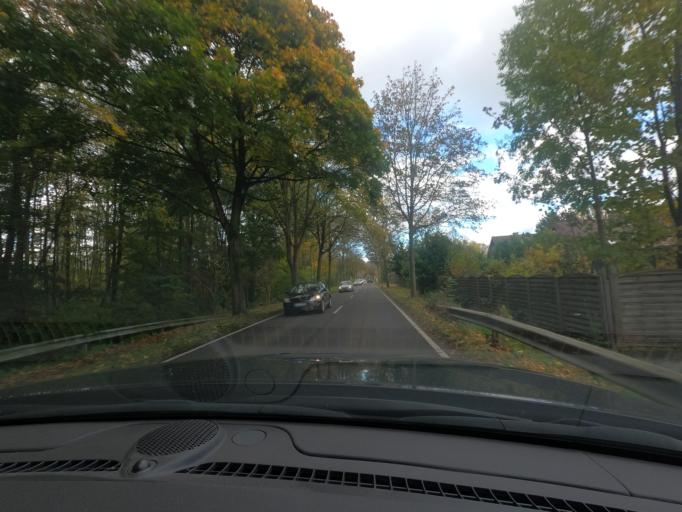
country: DE
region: North Rhine-Westphalia
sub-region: Regierungsbezirk Dusseldorf
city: Schwalmtal
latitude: 51.2584
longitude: 6.2912
